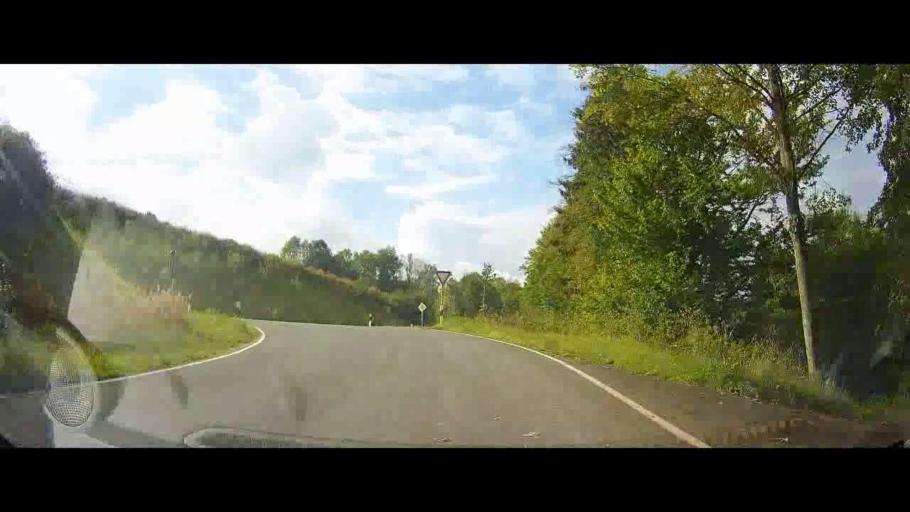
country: DE
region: Lower Saxony
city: Hardegsen
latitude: 51.6597
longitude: 9.7563
